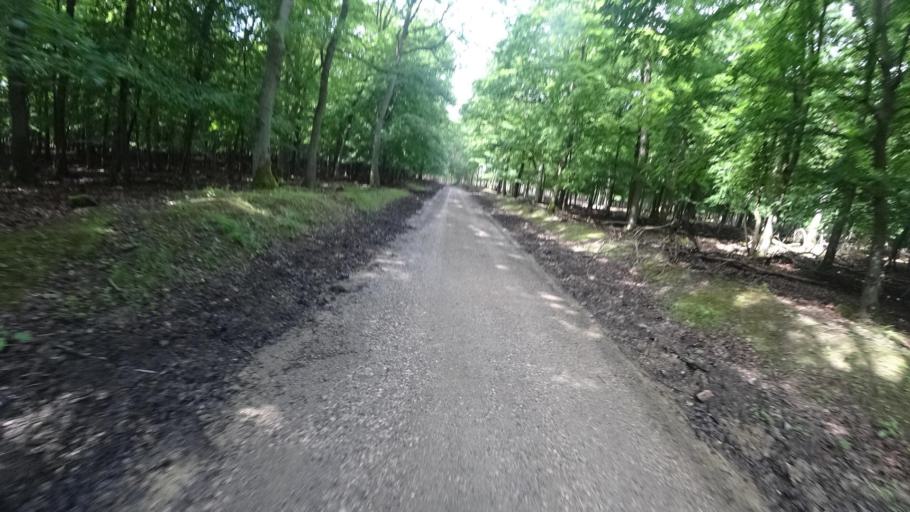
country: DE
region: Rheinland-Pfalz
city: Kalenborn
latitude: 50.5429
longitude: 6.9890
